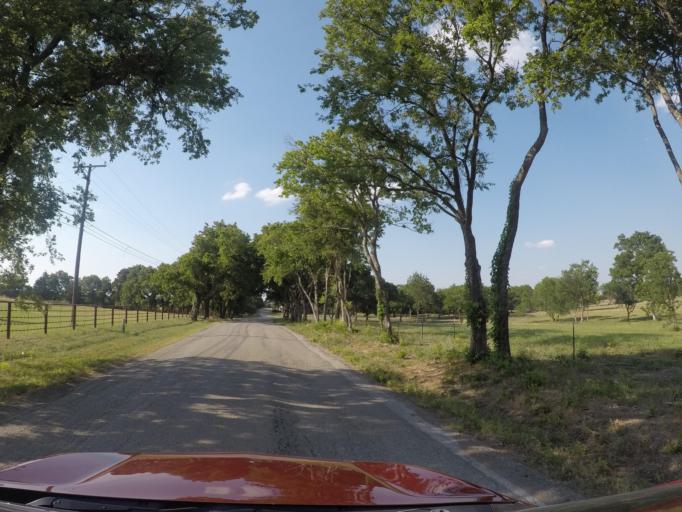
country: US
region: Texas
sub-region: Grayson County
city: Pottsboro
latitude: 33.8019
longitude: -96.6067
